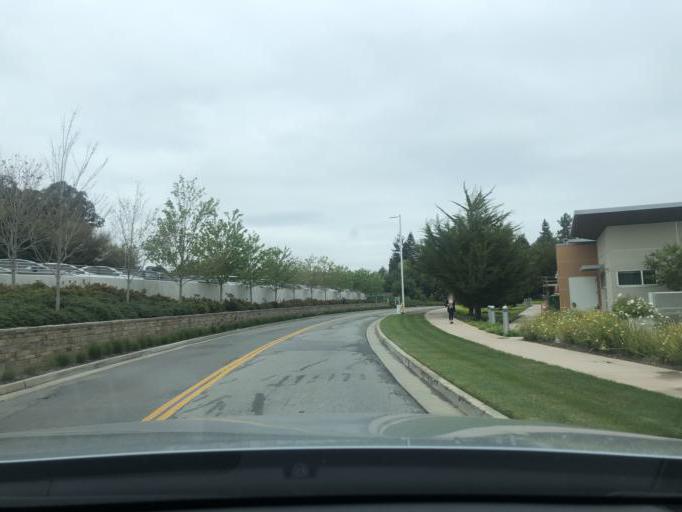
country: US
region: California
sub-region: Santa Clara County
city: Los Altos Hills
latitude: 37.4042
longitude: -122.1431
